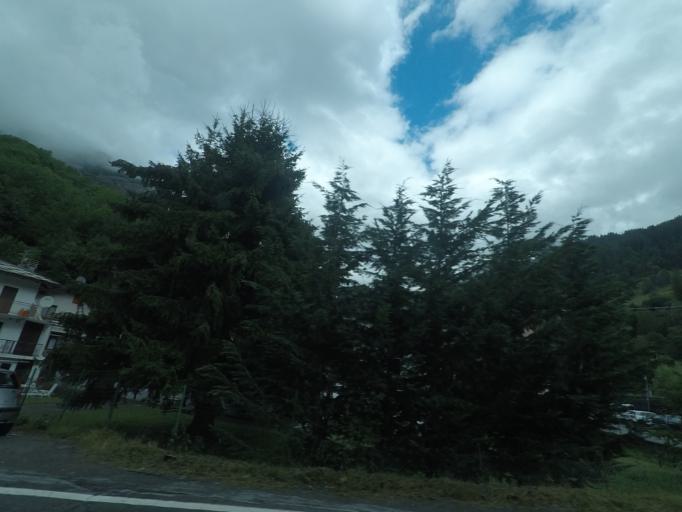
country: IT
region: Aosta Valley
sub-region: Valle d'Aosta
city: Valtournenche
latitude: 45.8686
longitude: 7.6158
